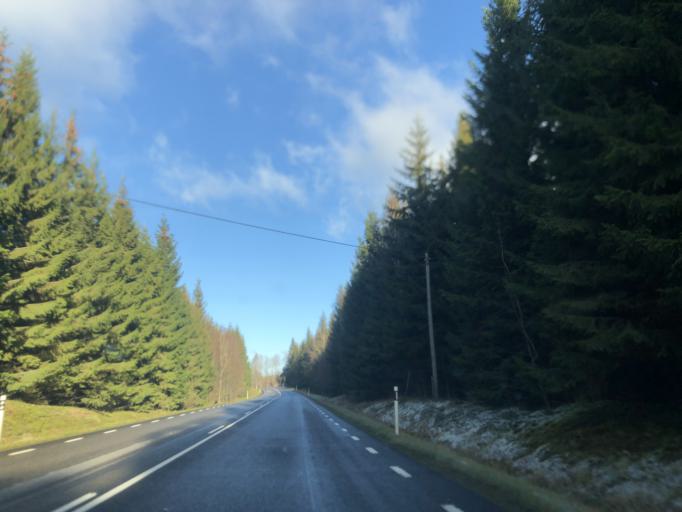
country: SE
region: Vaestra Goetaland
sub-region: Tranemo Kommun
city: Limmared
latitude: 57.6423
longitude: 13.4436
